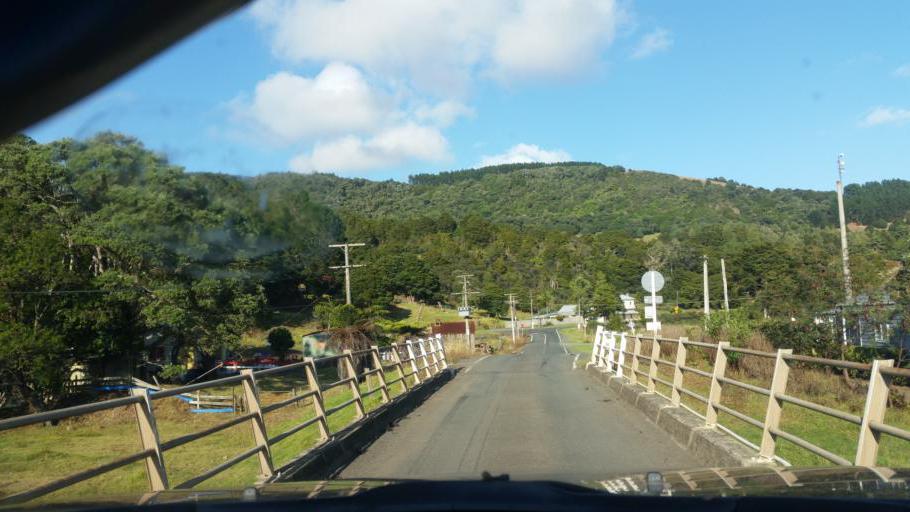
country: NZ
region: Northland
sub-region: Kaipara District
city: Dargaville
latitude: -35.7693
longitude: 173.6983
